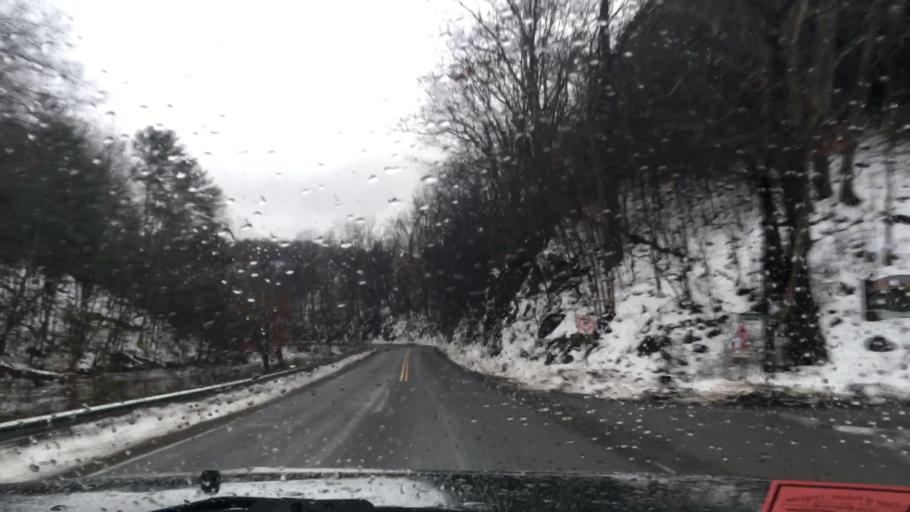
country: US
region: Virginia
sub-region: Pulaski County
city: Dublin
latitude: 37.0075
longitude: -80.6859
